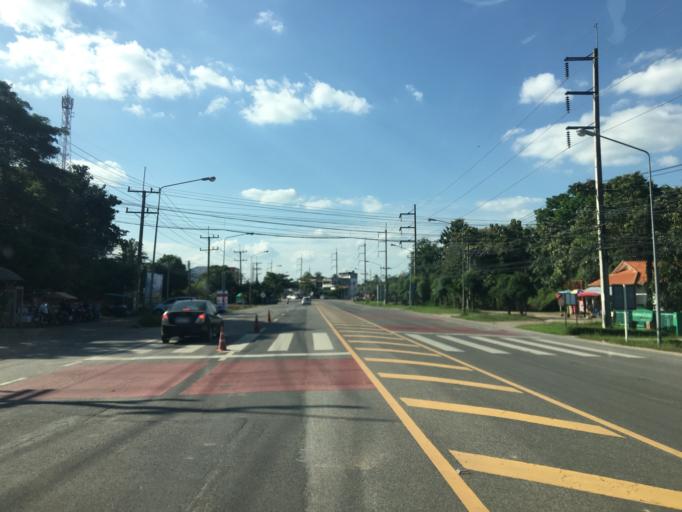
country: TH
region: Phayao
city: Chun
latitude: 19.3378
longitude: 100.1315
